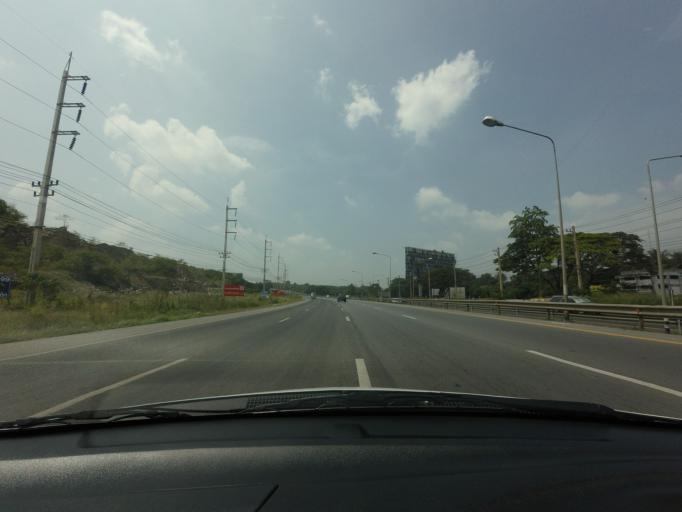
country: TH
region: Nakhon Ratchasima
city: Pak Chong
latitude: 14.6574
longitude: 101.3720
